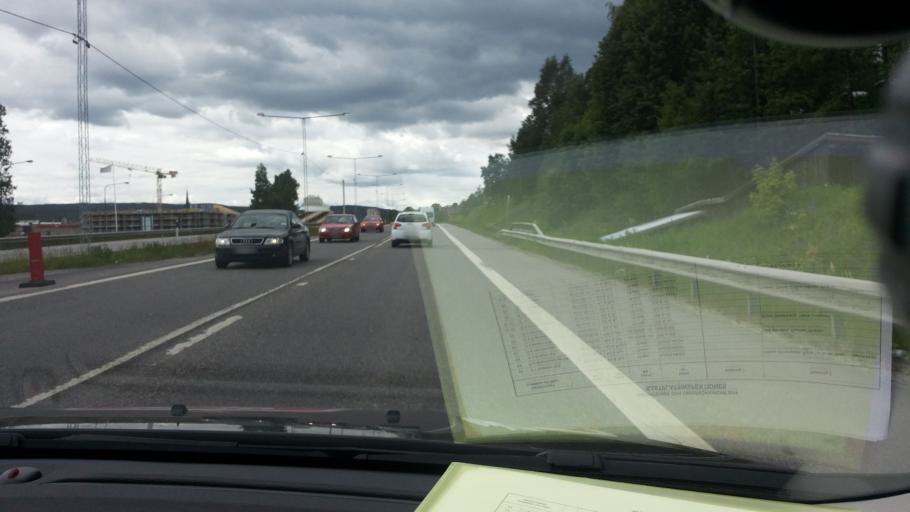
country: SE
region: Vaesternorrland
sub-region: Sundsvalls Kommun
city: Sundsvall
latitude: 62.3952
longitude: 17.3266
